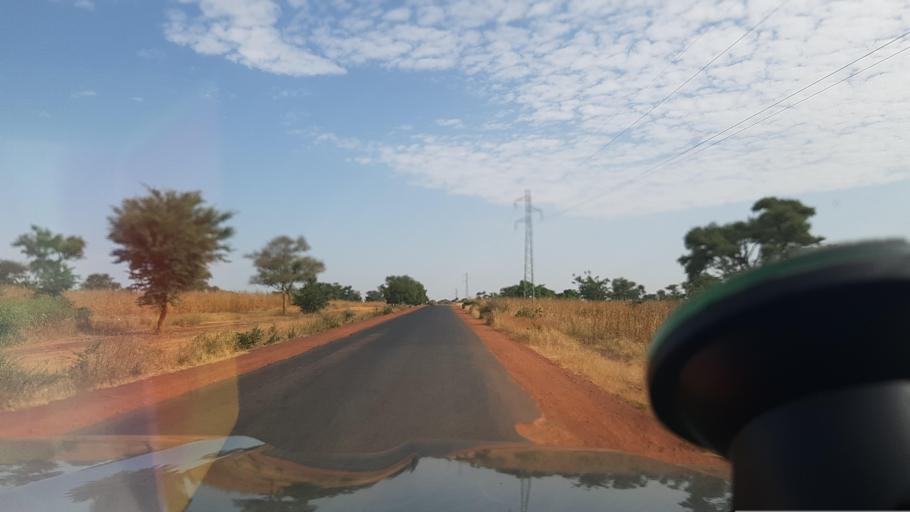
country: ML
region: Segou
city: Markala
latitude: 13.5657
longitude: -6.1094
